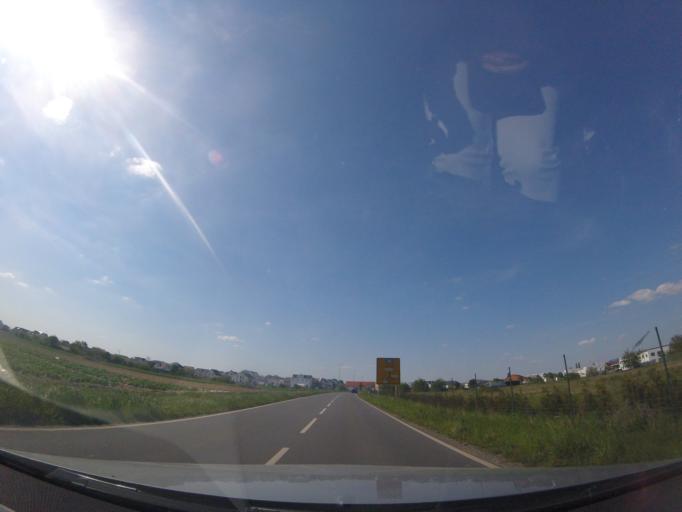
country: DE
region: Hesse
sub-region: Regierungsbezirk Darmstadt
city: Buttelborn
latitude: 49.8916
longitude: 8.5230
